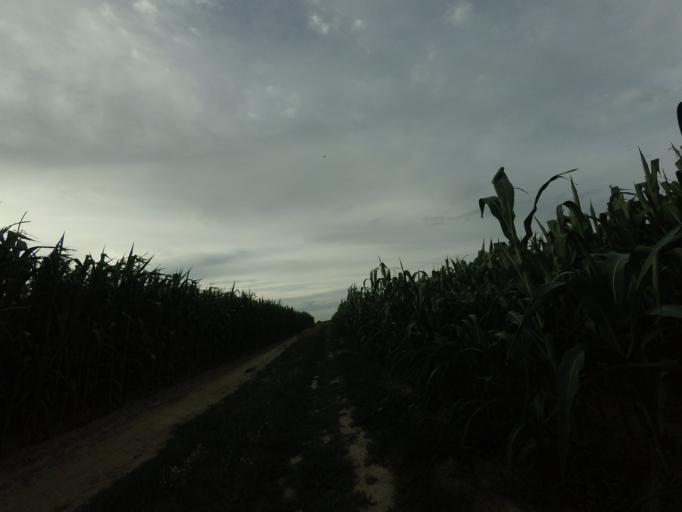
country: BE
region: Flanders
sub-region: Provincie Vlaams-Brabant
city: Grimbergen
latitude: 50.9651
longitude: 4.3654
